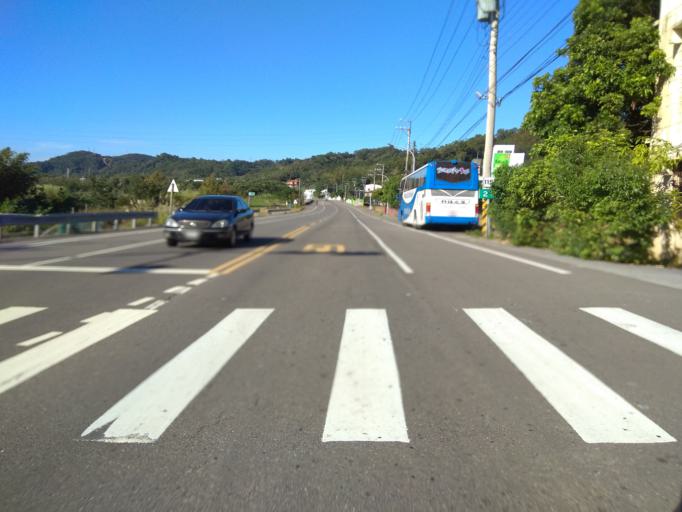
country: TW
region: Taiwan
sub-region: Hsinchu
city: Zhubei
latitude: 24.8482
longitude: 121.1125
